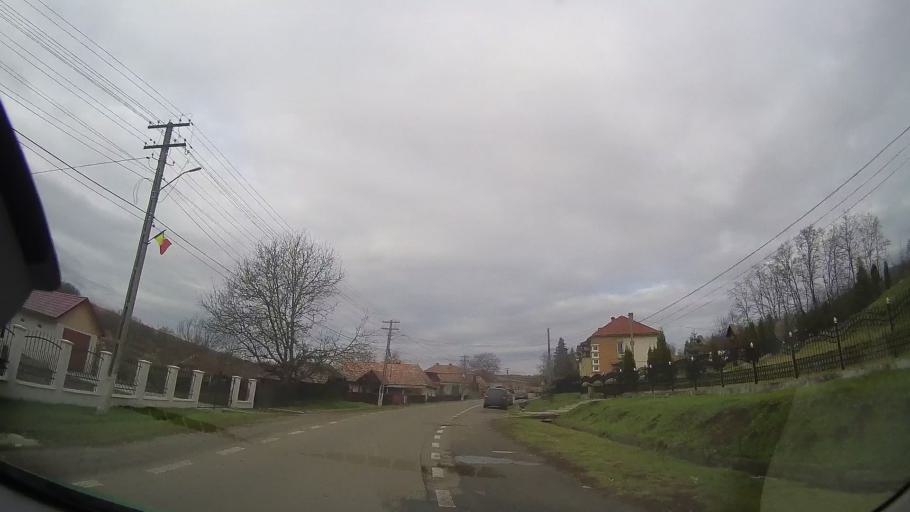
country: RO
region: Mures
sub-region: Comuna Cozma
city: Cozma
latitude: 46.8080
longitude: 24.5222
